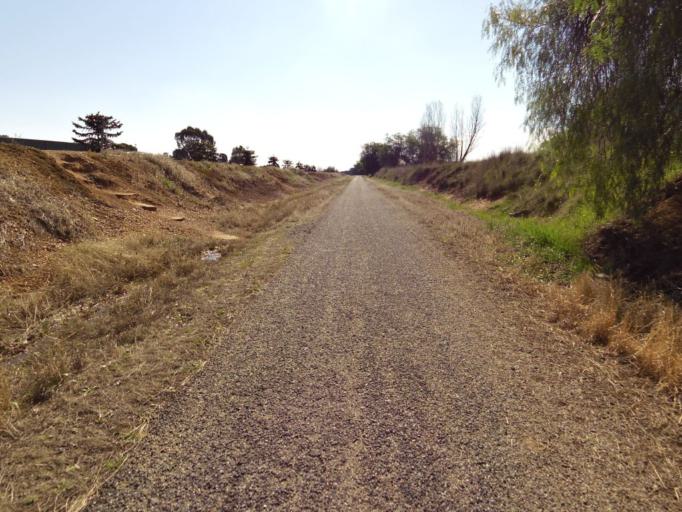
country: AU
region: New South Wales
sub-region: Corowa Shire
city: Corowa
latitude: -36.0519
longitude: 146.4613
